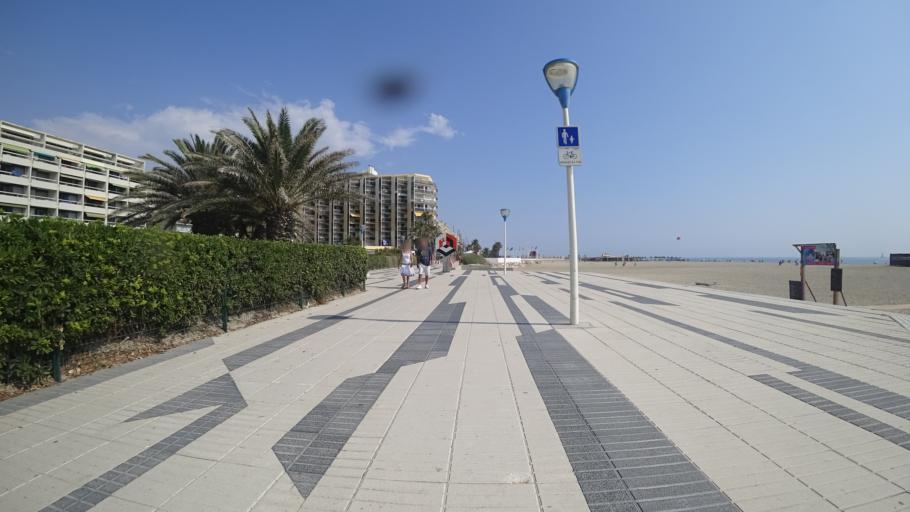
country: FR
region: Languedoc-Roussillon
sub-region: Departement des Pyrenees-Orientales
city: Canet-en-Roussillon
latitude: 42.6784
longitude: 3.0341
